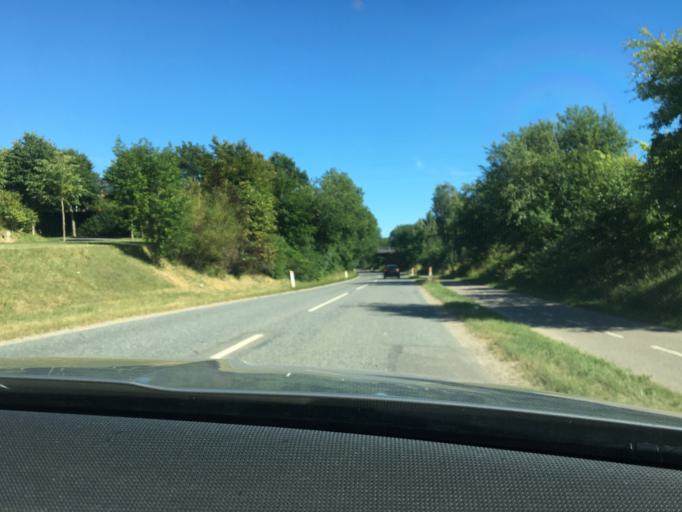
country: DK
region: Central Jutland
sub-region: Syddjurs Kommune
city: Hornslet
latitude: 56.3061
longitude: 10.3515
